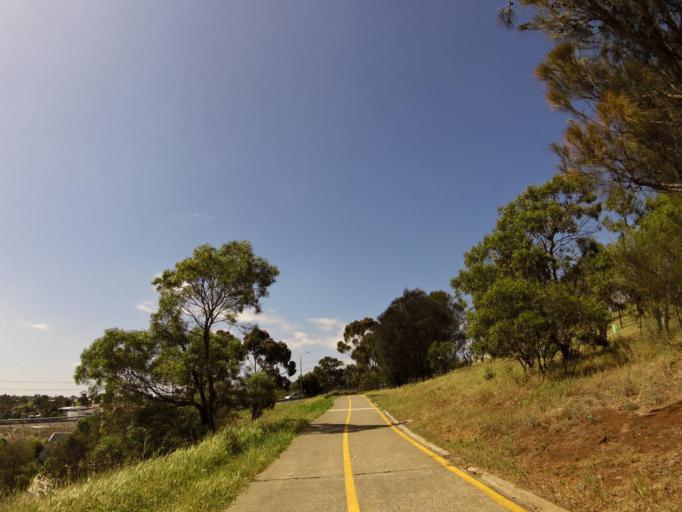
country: AU
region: Victoria
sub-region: Moonee Valley
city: Essendon West
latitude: -37.7538
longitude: 144.8806
